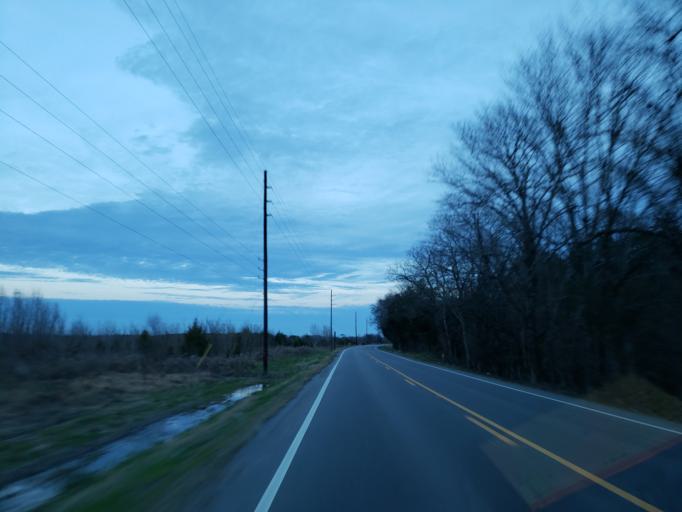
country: US
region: Alabama
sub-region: Sumter County
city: Livingston
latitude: 32.8091
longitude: -88.2897
